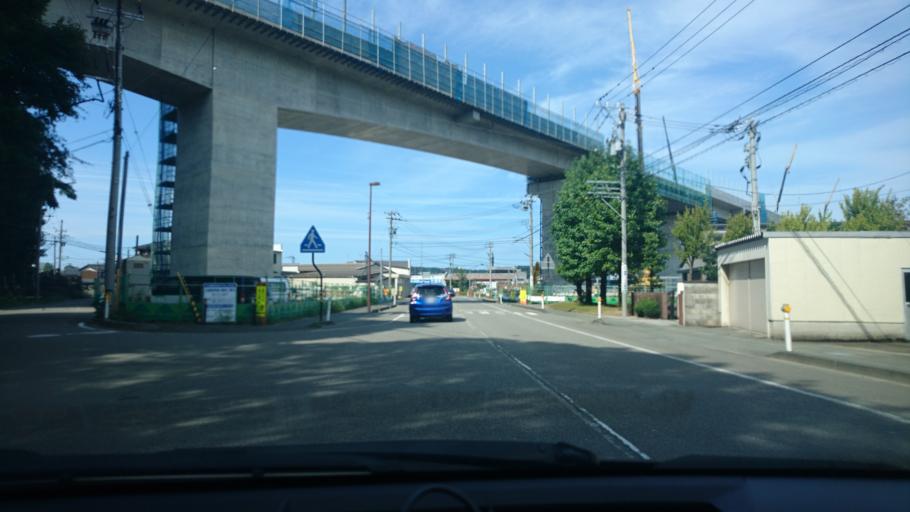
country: JP
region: Fukui
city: Maruoka
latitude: 36.2994
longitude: 136.3181
